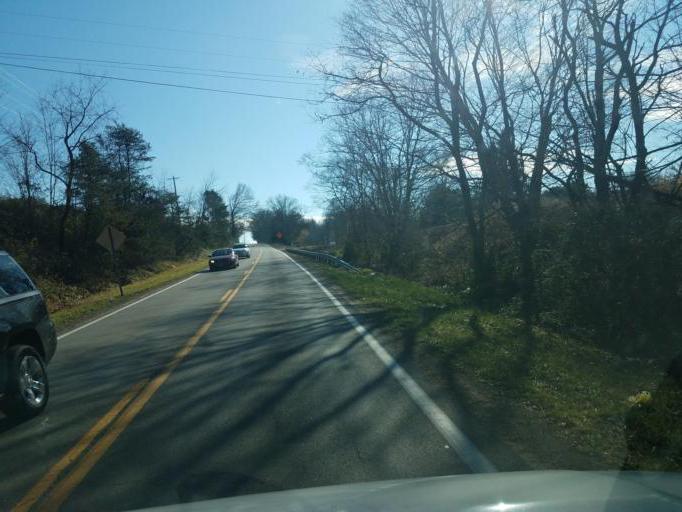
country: US
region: Ohio
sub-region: Scioto County
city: Sciotodale
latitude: 38.8493
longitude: -82.8556
